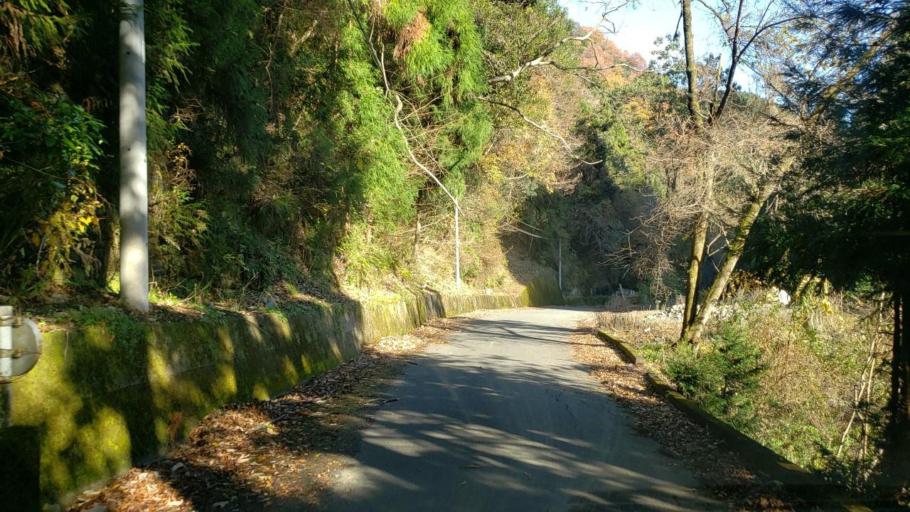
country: JP
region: Tokushima
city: Wakimachi
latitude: 33.9908
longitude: 133.9962
